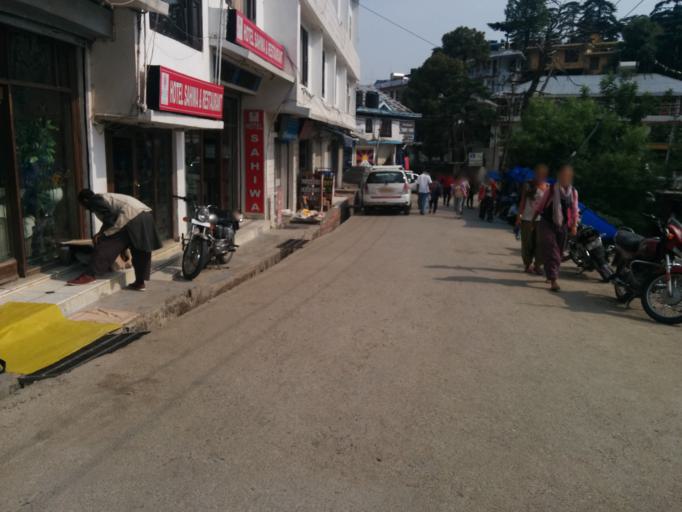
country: IN
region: Himachal Pradesh
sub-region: Kangra
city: Dharmsala
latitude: 32.2335
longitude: 76.3245
